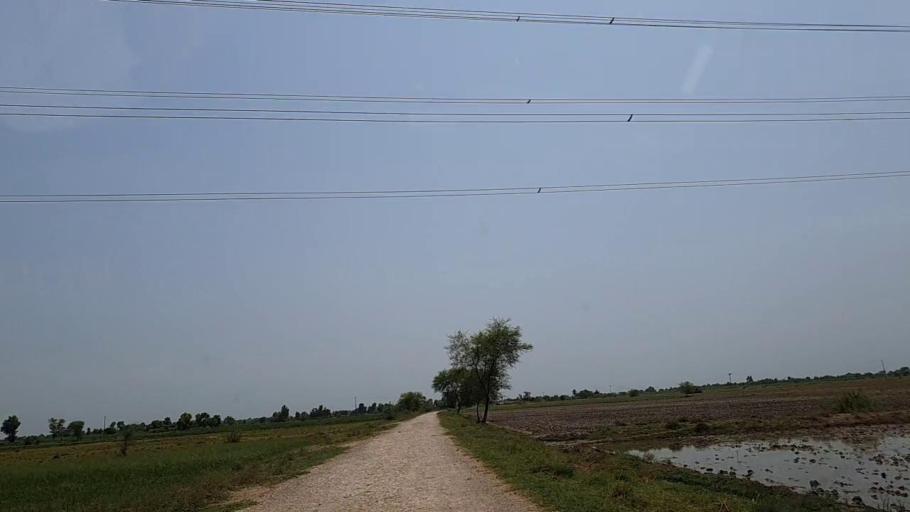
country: PK
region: Sindh
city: Ghotki
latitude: 27.9938
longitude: 69.4106
